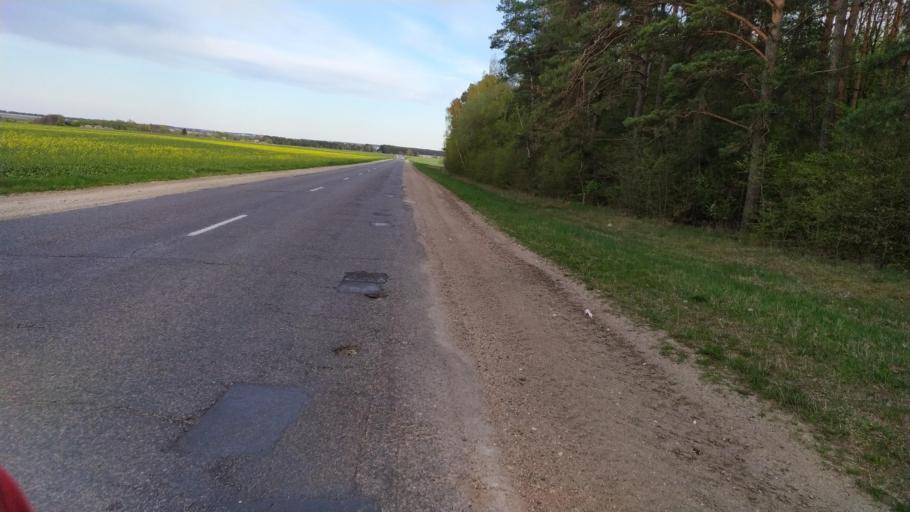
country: BY
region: Brest
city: Kamyanyets
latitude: 52.4152
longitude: 23.7066
